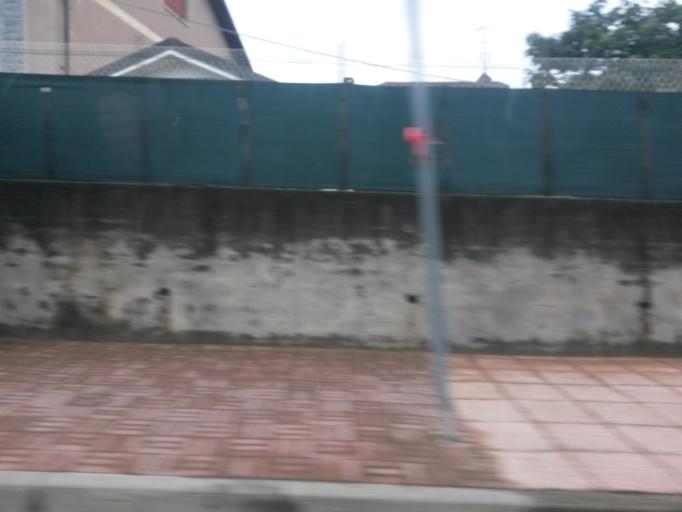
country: IT
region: Piedmont
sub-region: Provincia di Torino
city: Rosta
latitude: 45.0701
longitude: 7.4618
